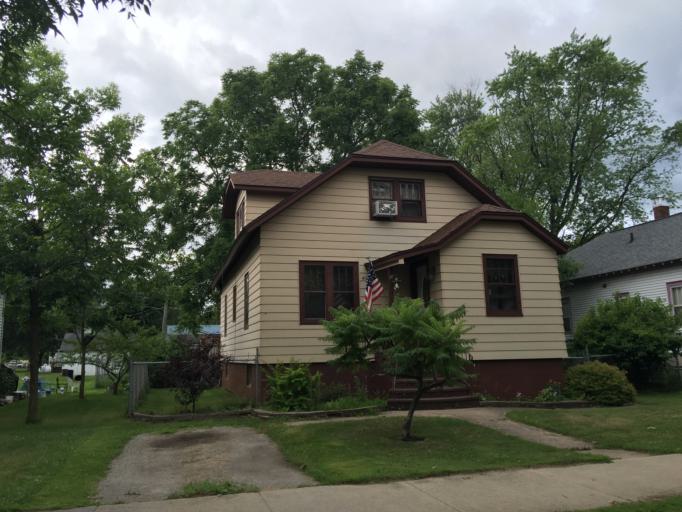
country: US
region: Michigan
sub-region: Menominee County
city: Menominee
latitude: 45.0894
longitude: -87.6076
